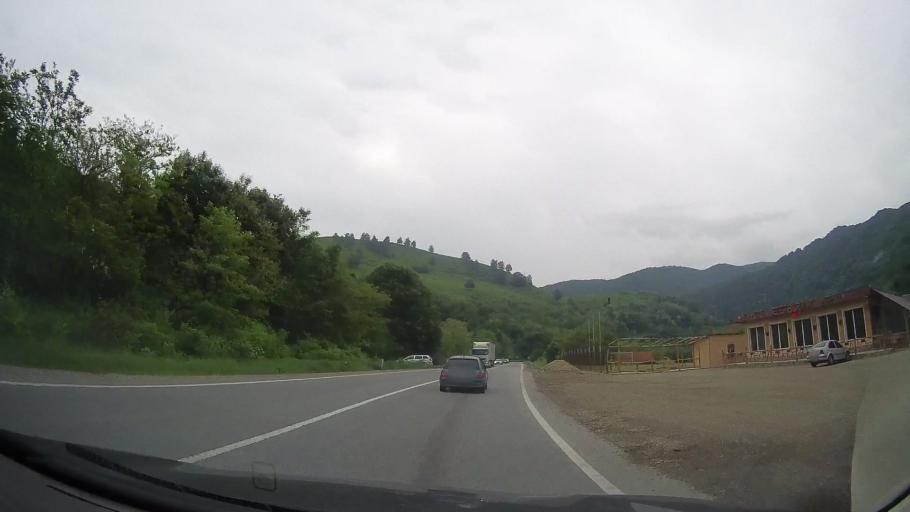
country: RO
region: Caras-Severin
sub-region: Comuna Armenis
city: Armenis
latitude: 45.2250
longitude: 22.3056
